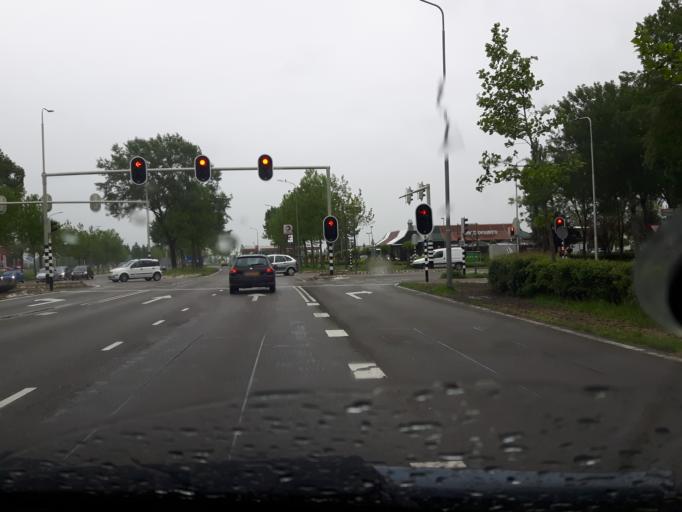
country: NL
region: Zeeland
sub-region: Gemeente Middelburg
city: Middelburg
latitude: 51.4843
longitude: 3.6246
